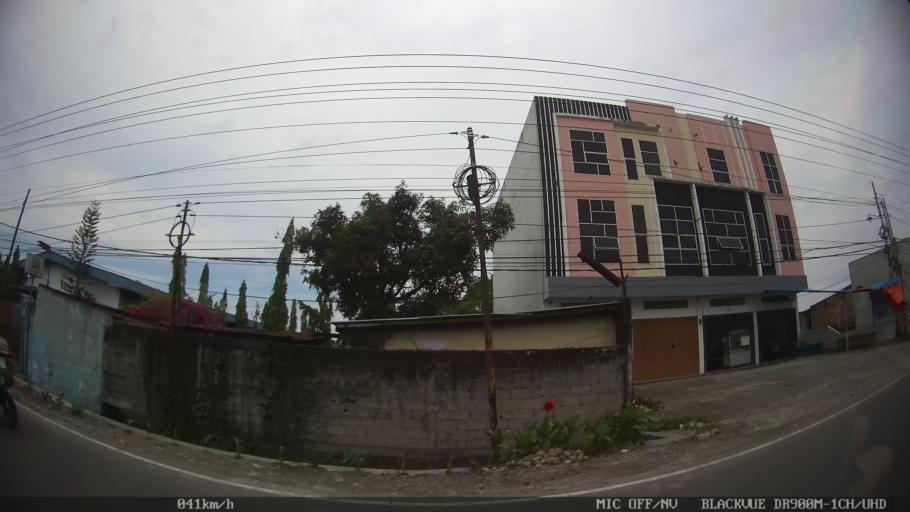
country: ID
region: North Sumatra
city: Sunggal
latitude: 3.5988
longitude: 98.5579
